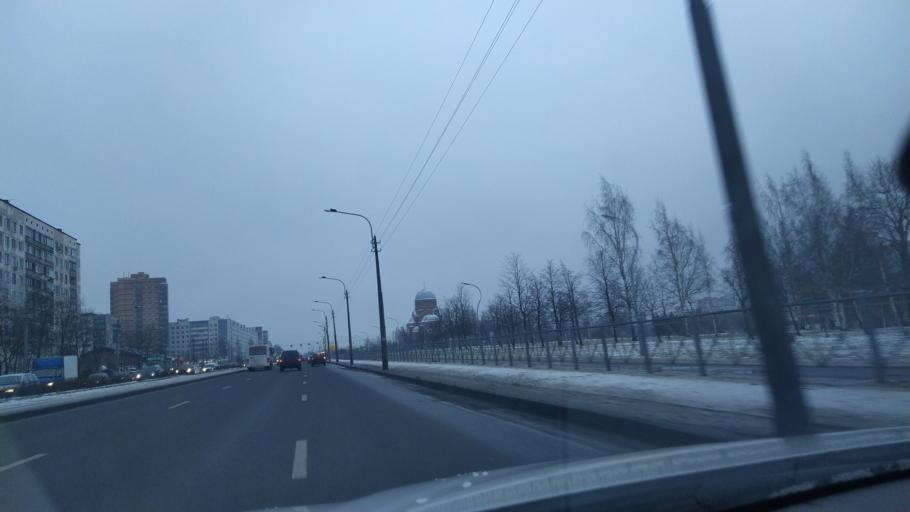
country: RU
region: St.-Petersburg
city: Grazhdanka
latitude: 60.0269
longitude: 30.4058
